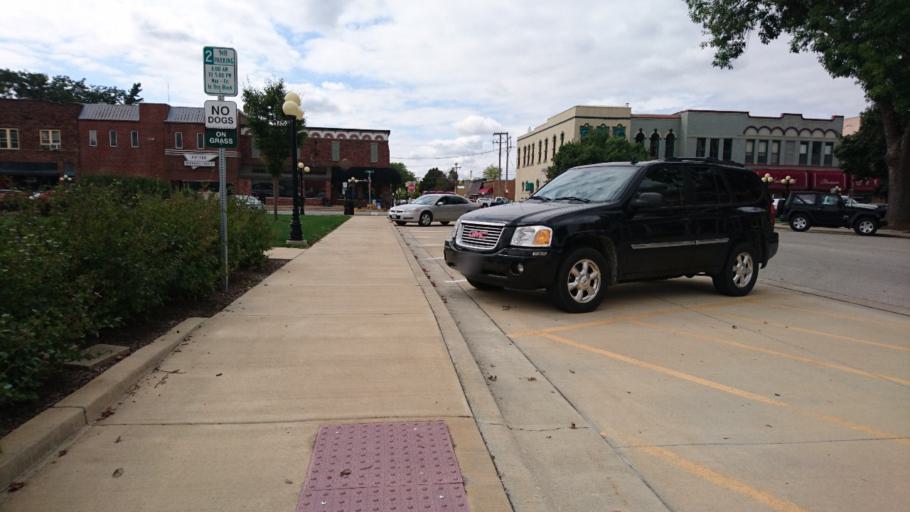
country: US
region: Illinois
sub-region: Livingston County
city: Pontiac
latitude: 40.8794
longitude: -88.6292
